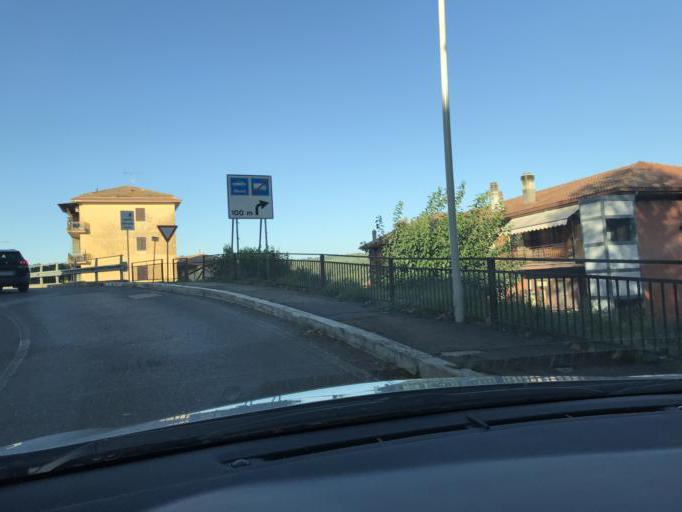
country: IT
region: Latium
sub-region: Provincia di Viterbo
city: Orte
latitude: 42.4584
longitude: 12.3883
